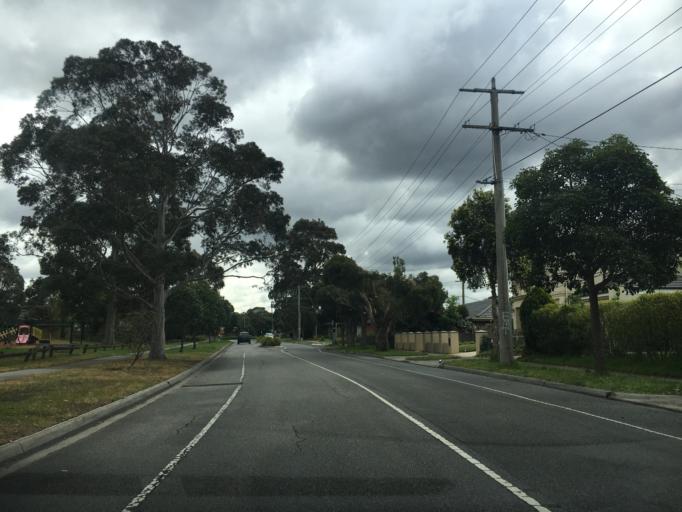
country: AU
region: Victoria
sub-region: Whitehorse
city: Vermont South
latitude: -37.8709
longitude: 145.1811
